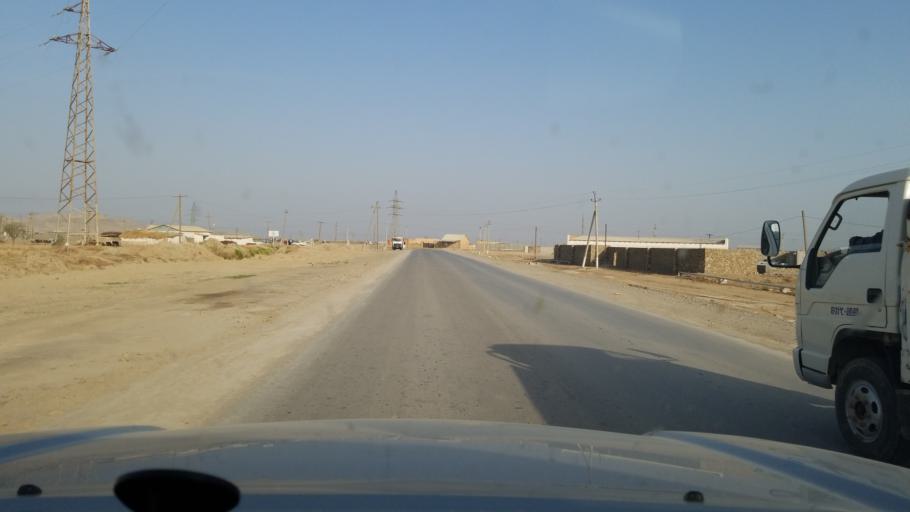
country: AF
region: Jowzjan
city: Qarqin
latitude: 37.5161
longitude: 66.0374
